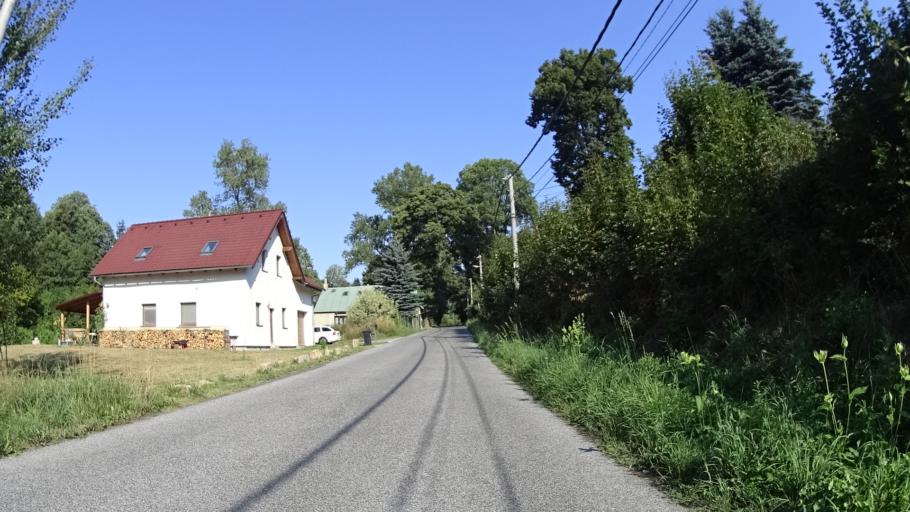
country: CZ
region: Liberecky
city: Hodkovice nad Mohelkou
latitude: 50.6969
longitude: 15.0985
